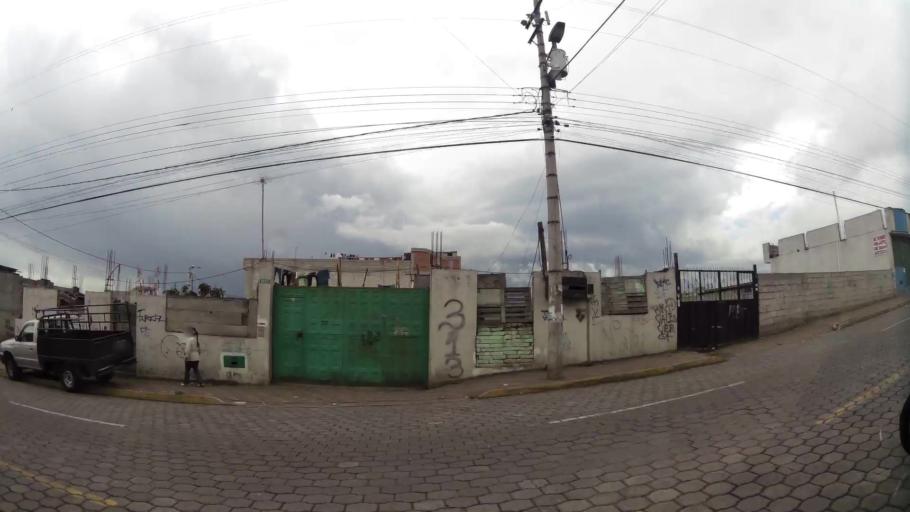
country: EC
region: Pichincha
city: Sangolqui
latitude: -0.3295
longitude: -78.5533
